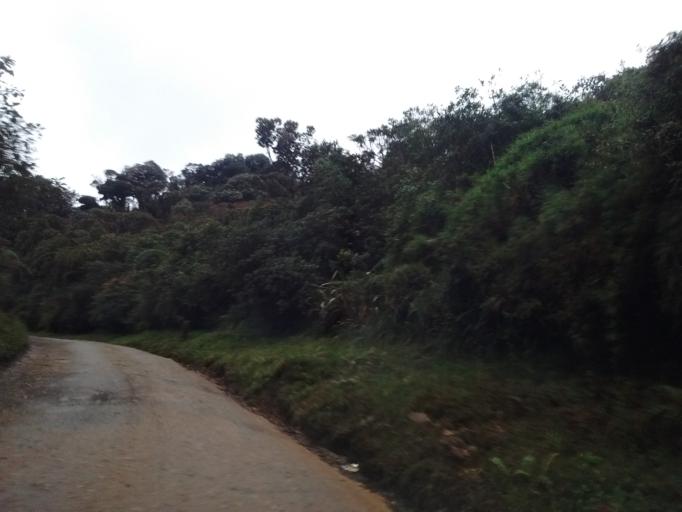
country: CO
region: Huila
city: Isnos
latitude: 2.1375
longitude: -76.3840
